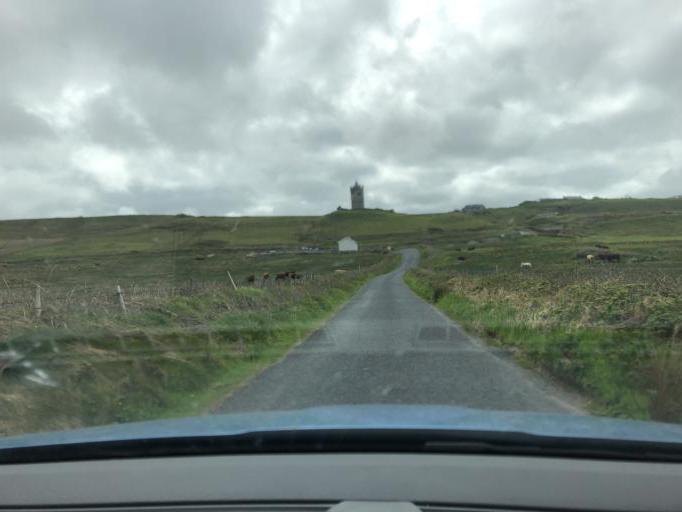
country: IE
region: Connaught
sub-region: County Galway
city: Bearna
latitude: 53.0072
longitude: -9.3884
